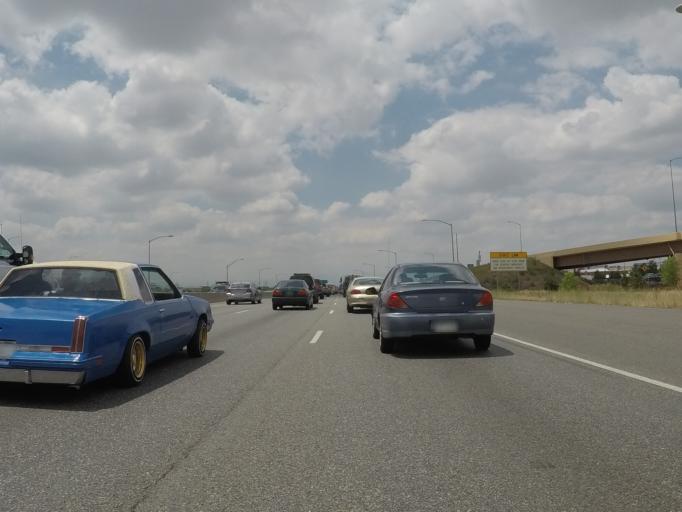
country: US
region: Colorado
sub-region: Adams County
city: Commerce City
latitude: 39.7776
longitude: -104.8862
